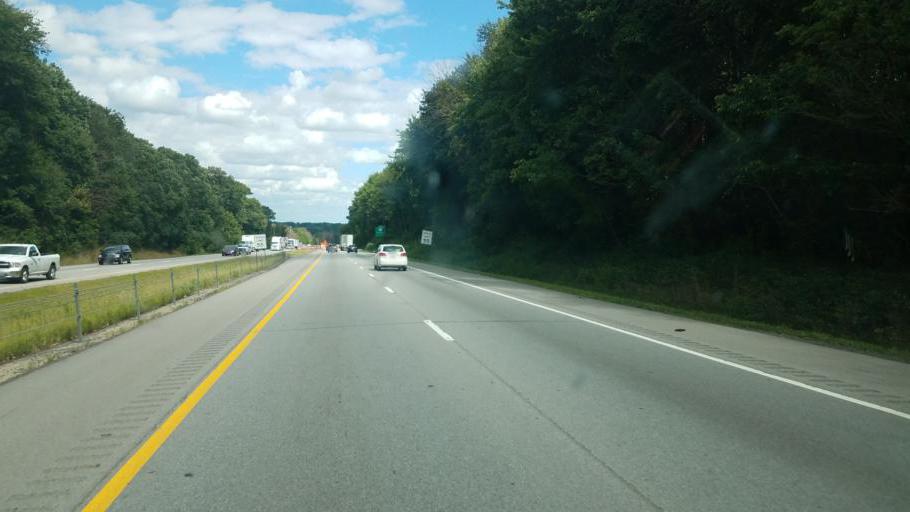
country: US
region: Ohio
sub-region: Medina County
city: Wadsworth
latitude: 41.0471
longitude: -81.7072
